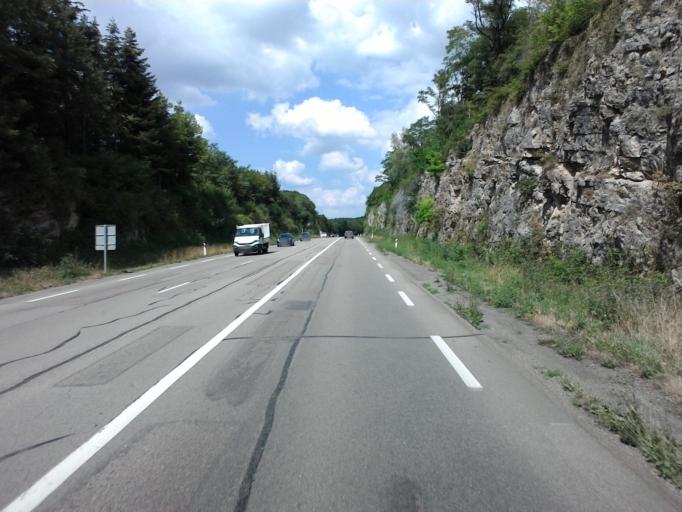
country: FR
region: Franche-Comte
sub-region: Departement du Jura
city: Mouchard
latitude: 46.9702
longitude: 5.8013
